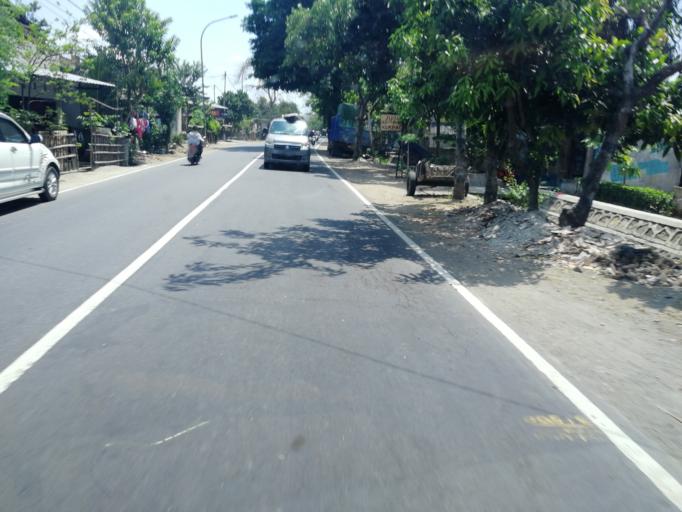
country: ID
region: West Nusa Tenggara
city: Jelateng Timur
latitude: -8.7068
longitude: 116.0850
